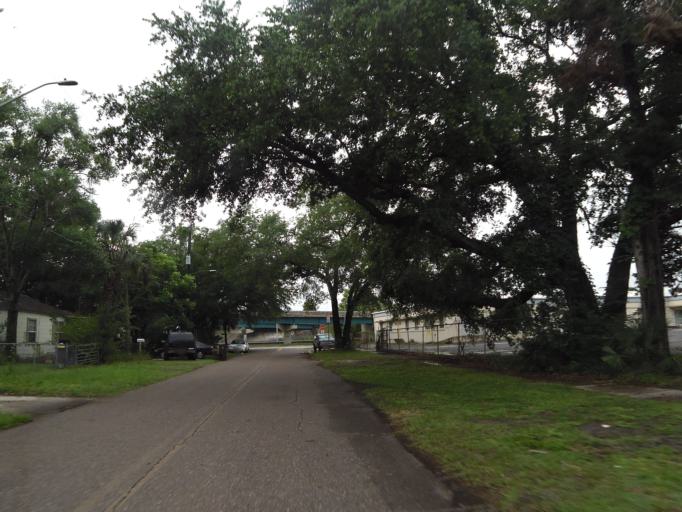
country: US
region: Florida
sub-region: Duval County
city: Jacksonville
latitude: 30.3309
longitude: -81.6354
